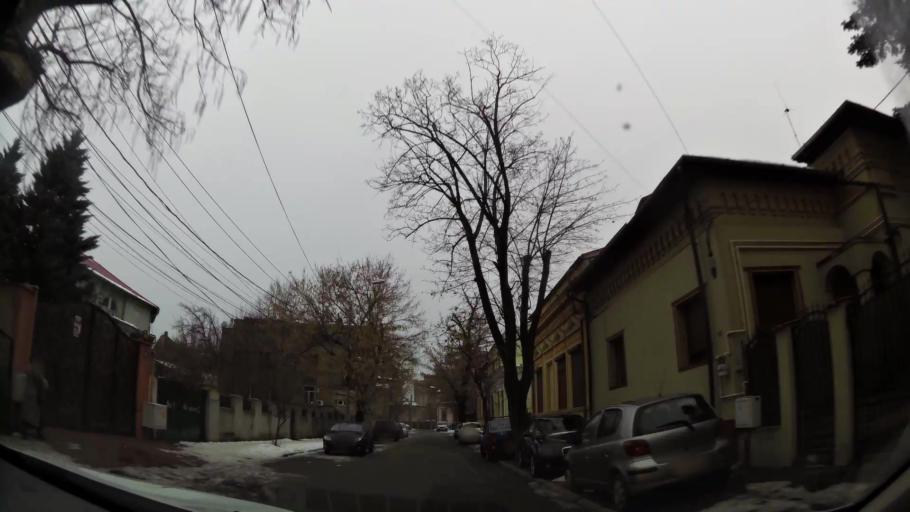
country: RO
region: Bucuresti
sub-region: Municipiul Bucuresti
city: Bucharest
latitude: 44.4342
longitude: 26.1138
